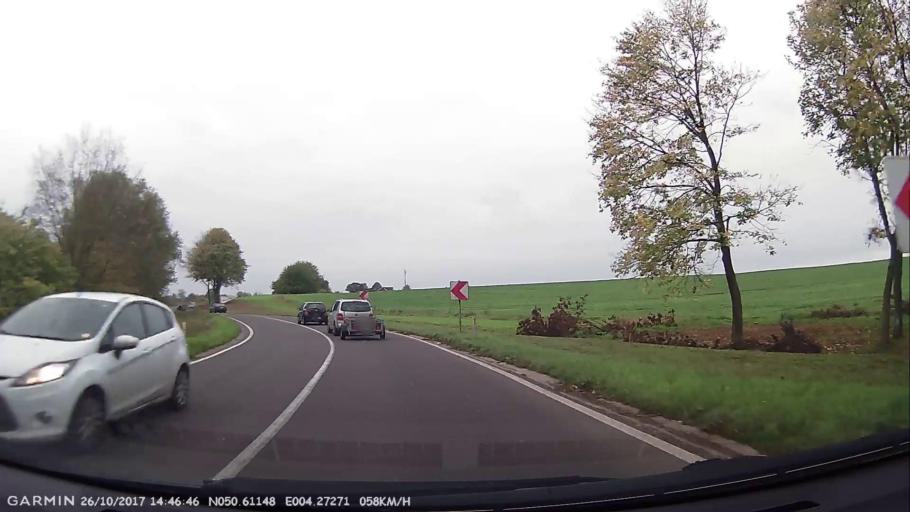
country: BE
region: Wallonia
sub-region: Province du Brabant Wallon
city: Ittre
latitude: 50.6116
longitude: 4.2723
